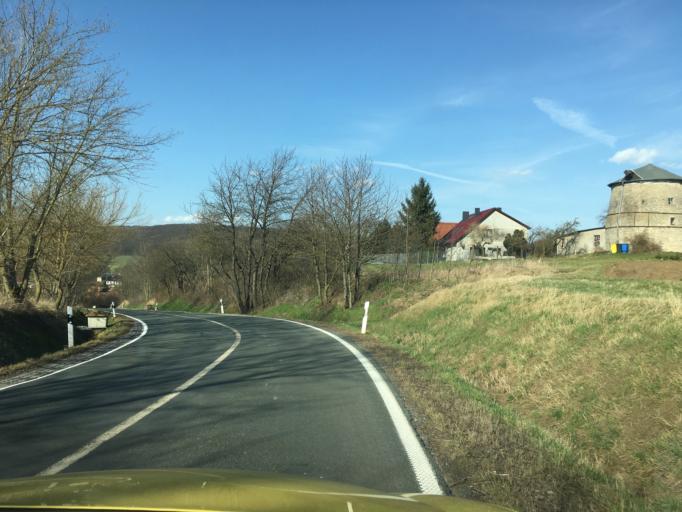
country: DE
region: Thuringia
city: Ostramondra
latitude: 51.1925
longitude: 11.3567
